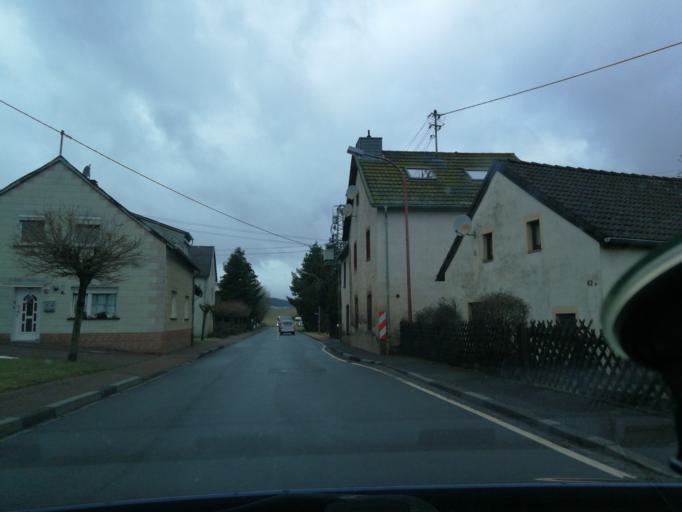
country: DE
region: Rheinland-Pfalz
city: Dreis-Bruck
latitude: 50.2658
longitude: 6.7891
